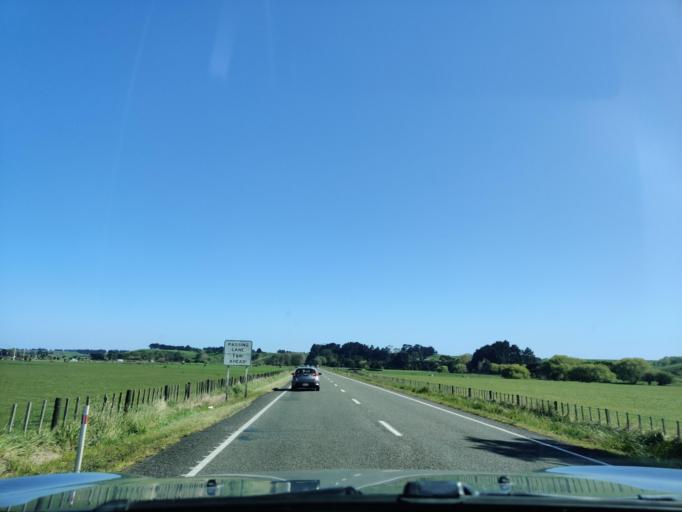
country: NZ
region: Manawatu-Wanganui
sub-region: Rangitikei District
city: Bulls
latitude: -40.0693
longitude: 175.2276
